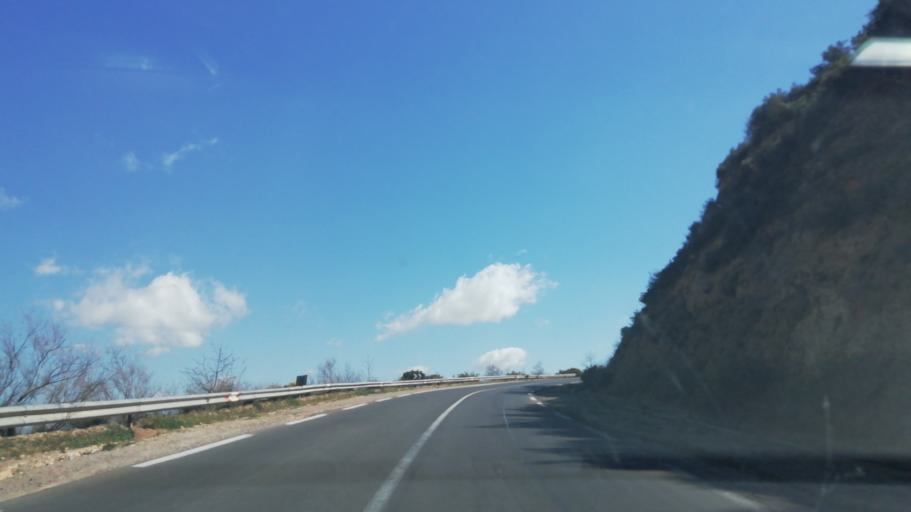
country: DZ
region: Mascara
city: Mascara
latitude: 35.4896
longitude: 0.1490
